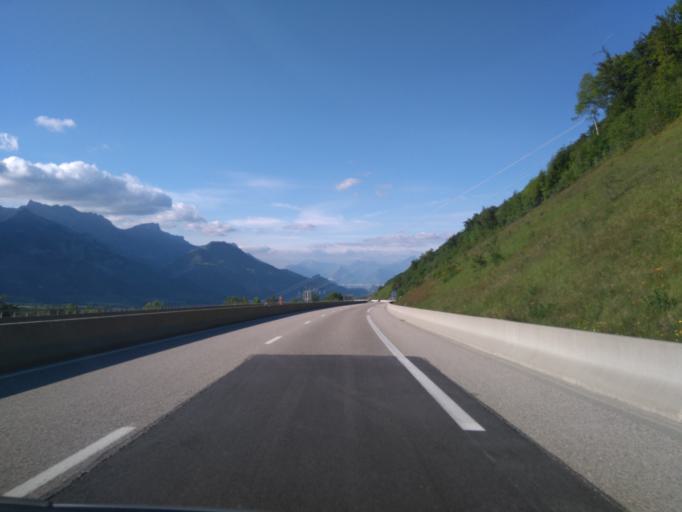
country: FR
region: Rhone-Alpes
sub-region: Departement de l'Isere
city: Le Gua
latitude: 44.9762
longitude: 5.6453
